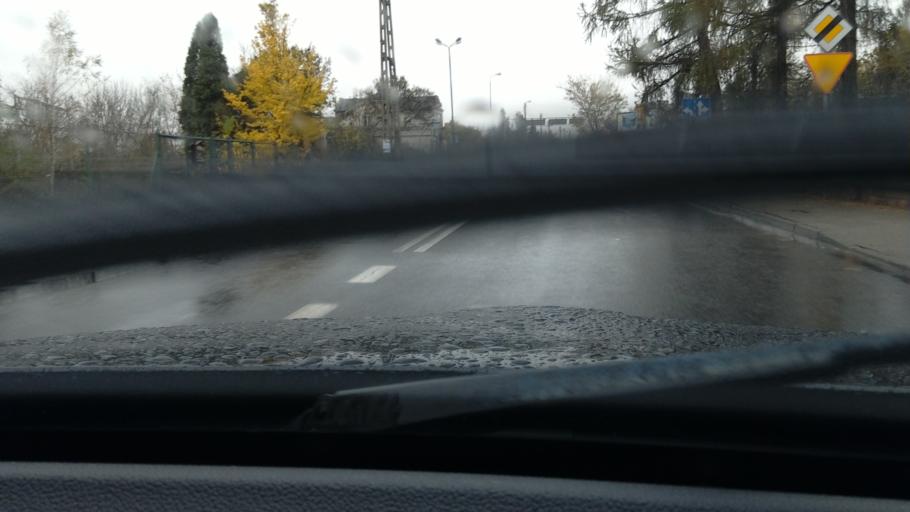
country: PL
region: Lodz Voivodeship
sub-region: Skierniewice
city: Skierniewice
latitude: 51.9541
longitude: 20.1336
